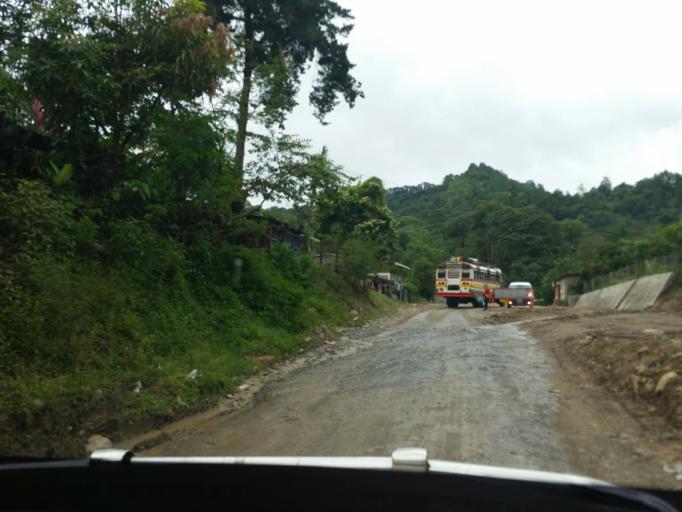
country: NI
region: Jinotega
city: Jinotega
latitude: 13.1526
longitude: -85.9276
